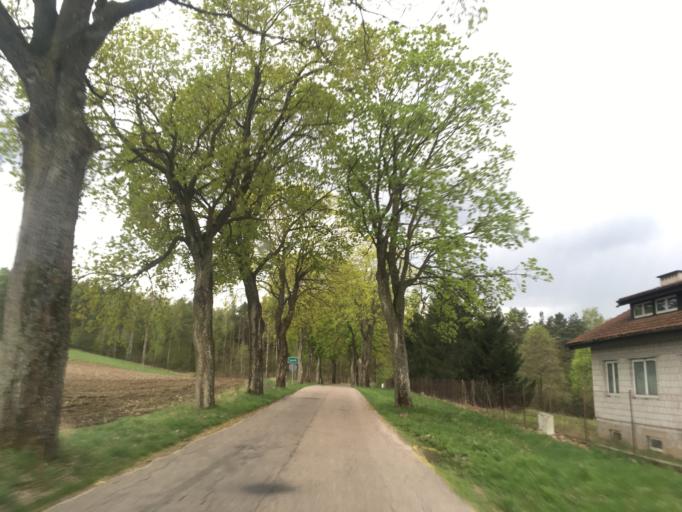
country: PL
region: Warmian-Masurian Voivodeship
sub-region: Powiat ostrodzki
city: Dabrowno
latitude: 53.4156
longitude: 20.0732
